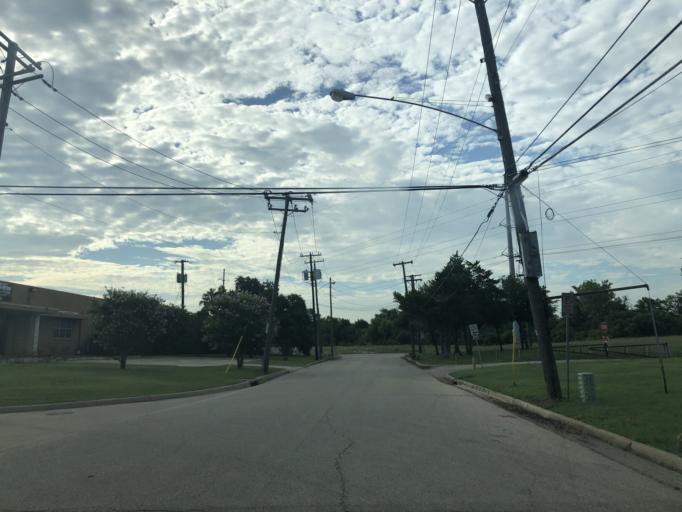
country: US
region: Texas
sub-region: Dallas County
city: Irving
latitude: 32.8148
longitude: -96.8853
